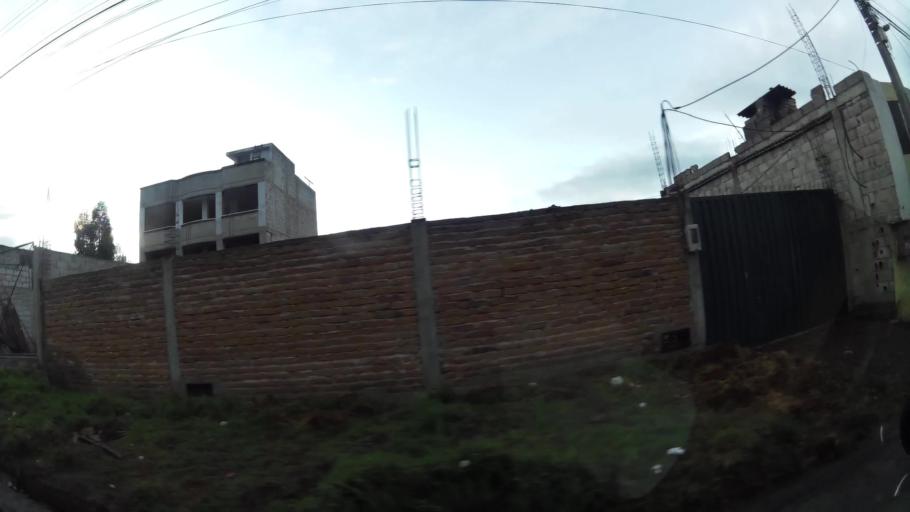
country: EC
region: Pichincha
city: Quito
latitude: -0.0960
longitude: -78.5276
